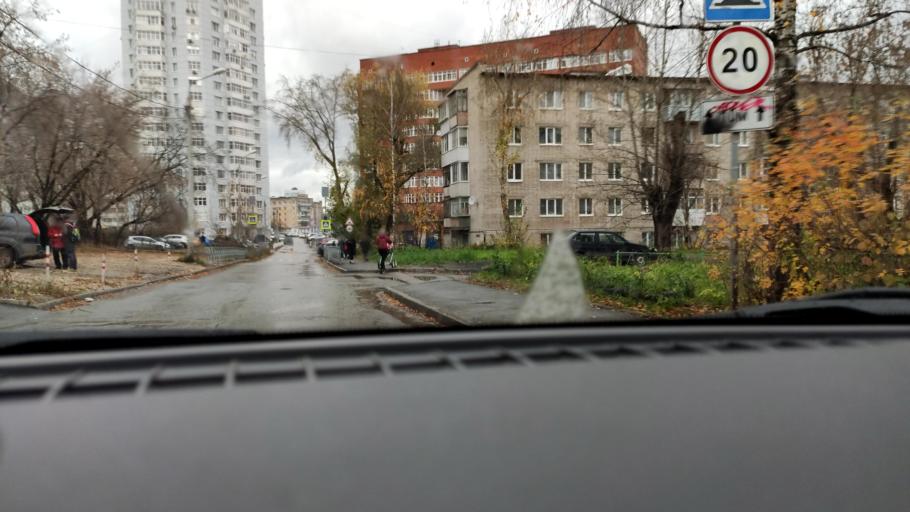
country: RU
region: Perm
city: Perm
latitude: 58.0035
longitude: 56.2719
